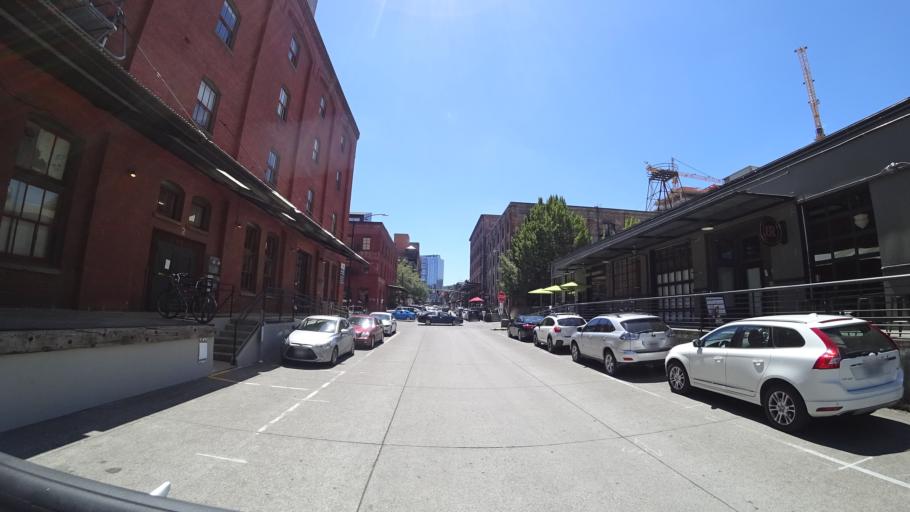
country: US
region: Oregon
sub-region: Multnomah County
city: Portland
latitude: 45.5276
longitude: -122.6843
